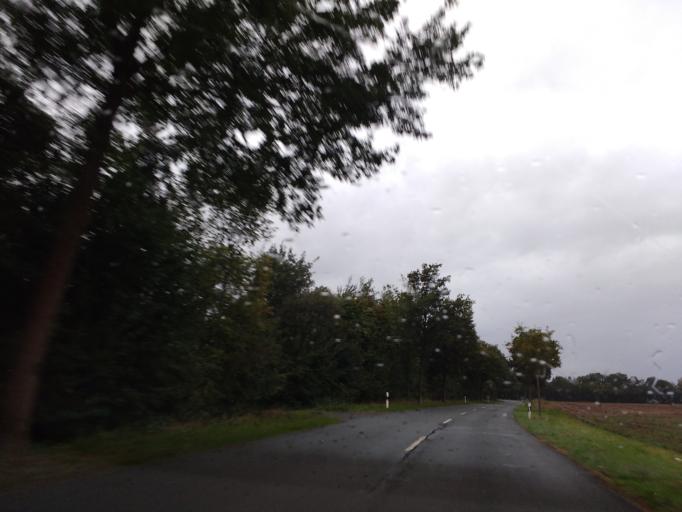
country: DE
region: North Rhine-Westphalia
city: Rietberg
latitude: 51.7280
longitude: 8.4391
